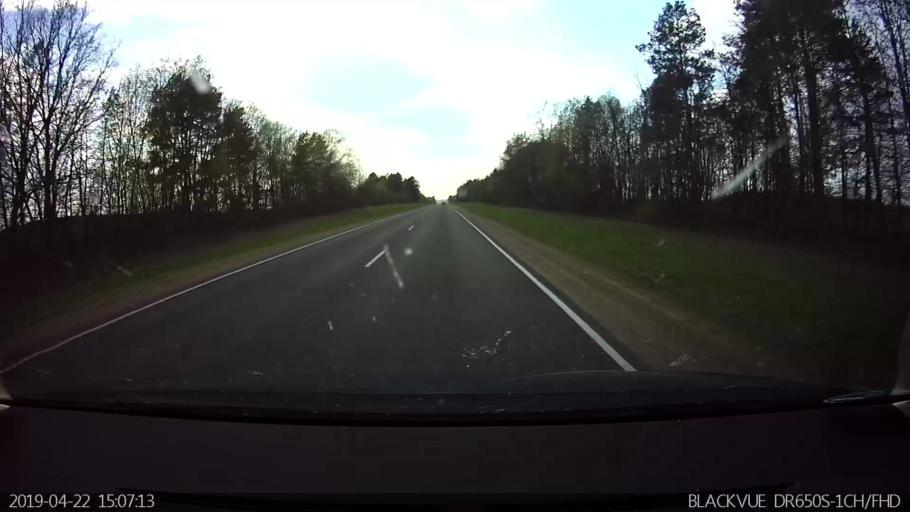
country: BY
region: Brest
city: Kamyanyets
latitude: 52.3294
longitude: 23.8144
